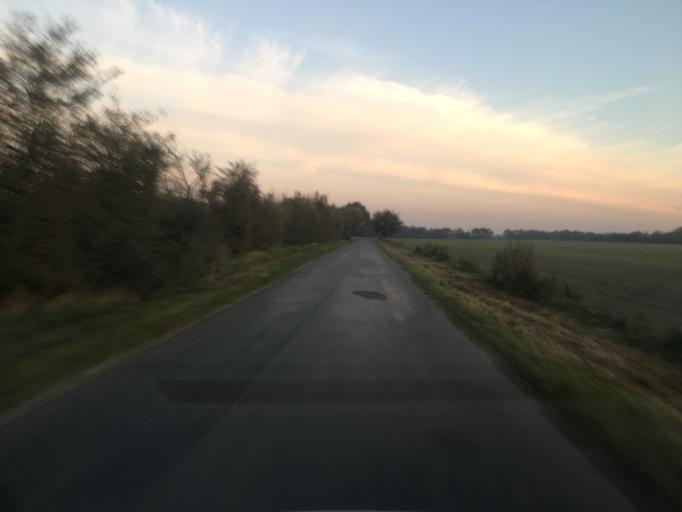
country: DE
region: Schleswig-Holstein
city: Bramstedtlund
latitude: 54.9795
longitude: 9.0670
